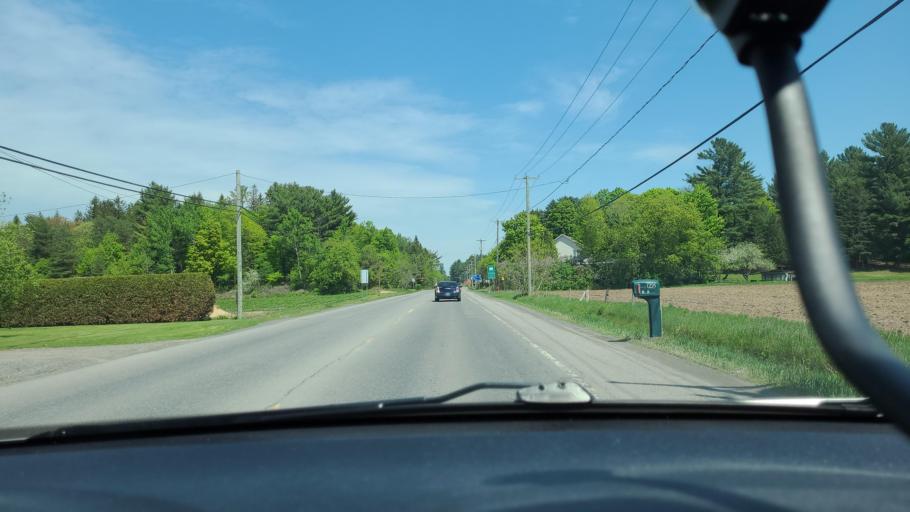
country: CA
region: Quebec
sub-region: Laurentides
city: Lachute
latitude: 45.6634
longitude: -74.3010
